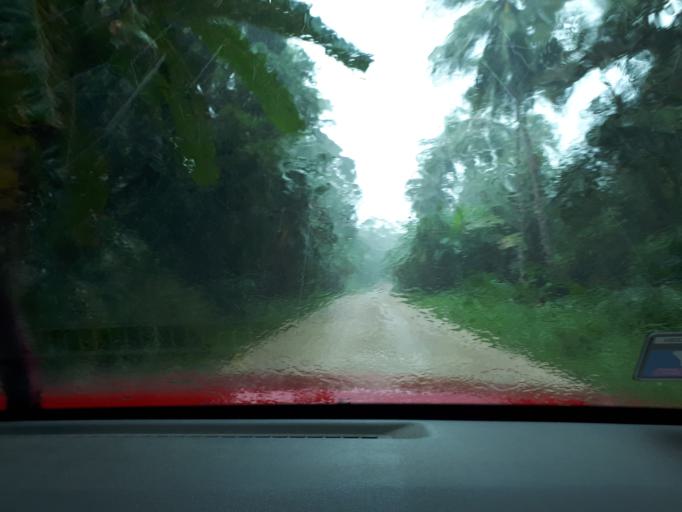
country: VU
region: Sanma
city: Luganville
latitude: -15.5587
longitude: 166.9949
